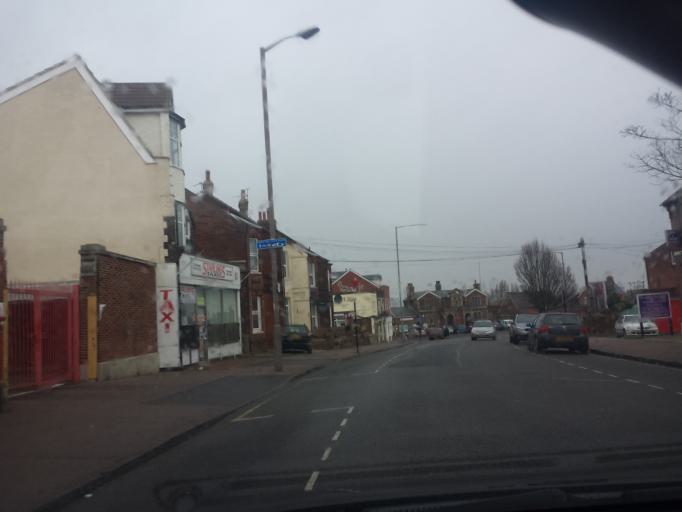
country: GB
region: England
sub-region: Essex
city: Dovercourt
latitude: 51.9377
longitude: 1.2803
